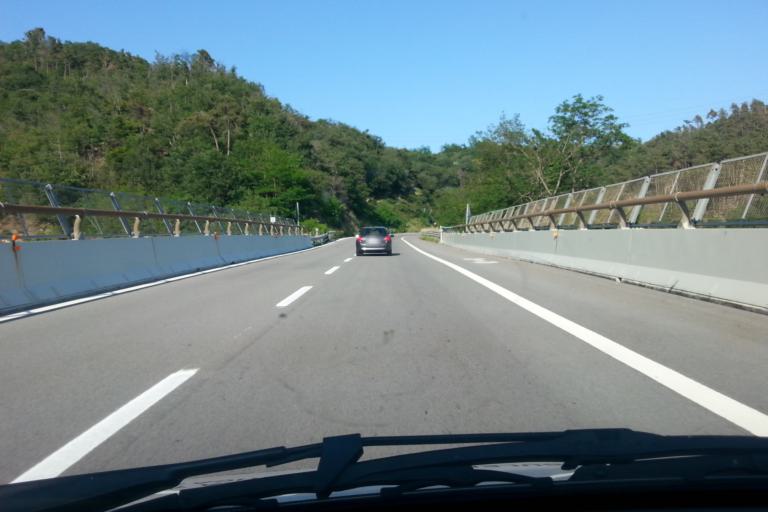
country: IT
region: Liguria
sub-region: Provincia di Savona
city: Quiliano
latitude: 44.2989
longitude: 8.4180
